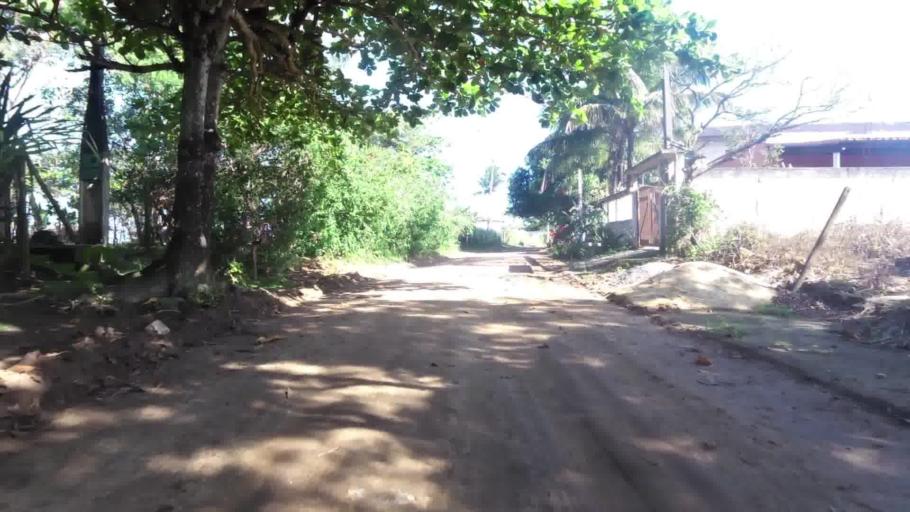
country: BR
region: Espirito Santo
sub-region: Piuma
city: Piuma
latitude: -20.8188
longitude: -40.6156
